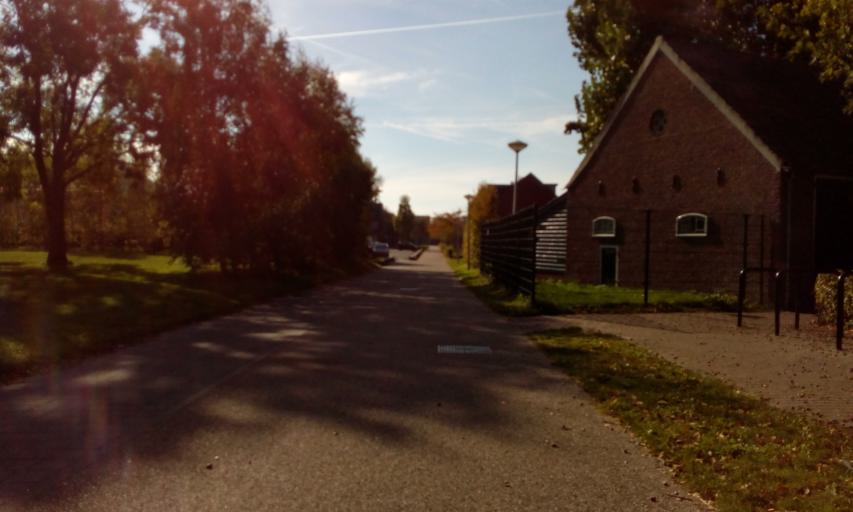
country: NL
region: Utrecht
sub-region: Stichtse Vecht
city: Spechtenkamp
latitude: 52.0804
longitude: 5.0229
